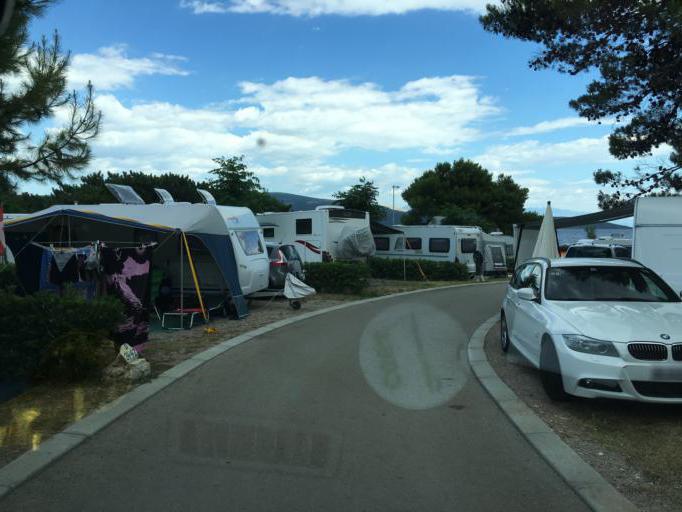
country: HR
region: Primorsko-Goranska
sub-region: Grad Krk
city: Krk
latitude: 45.0207
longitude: 14.5733
